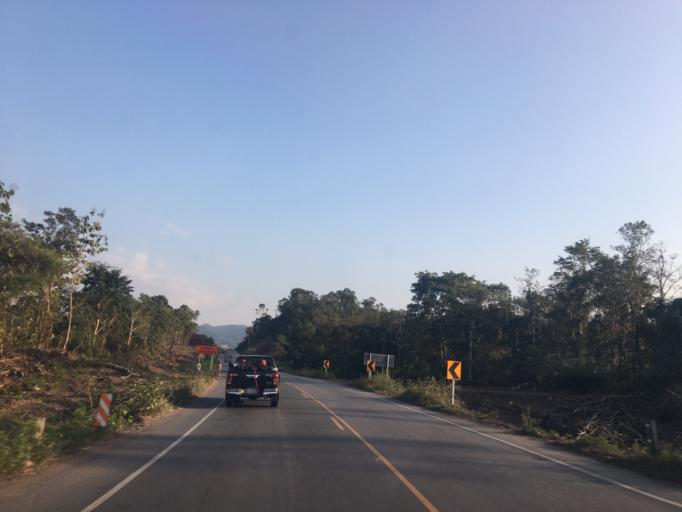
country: TH
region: Lampang
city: Ngao
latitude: 18.6240
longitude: 100.0186
